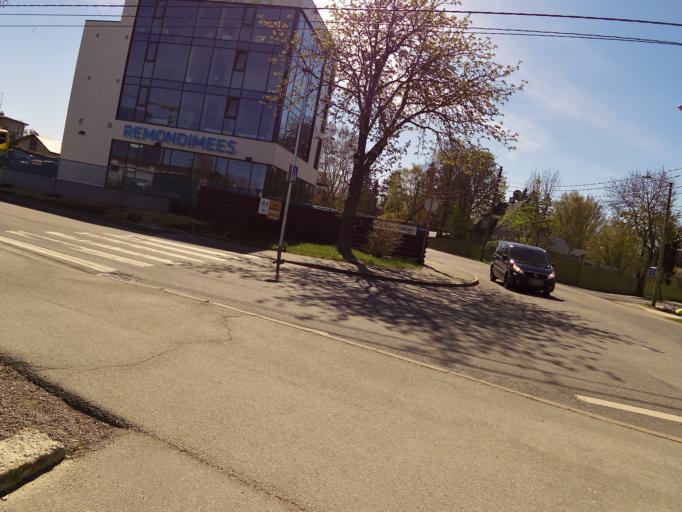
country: EE
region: Harju
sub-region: Tallinna linn
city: Tallinn
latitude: 59.4167
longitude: 24.7534
